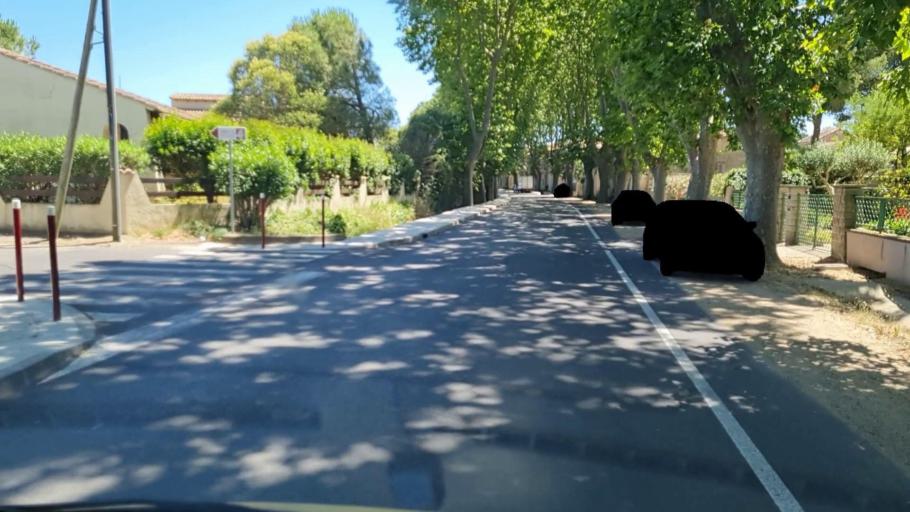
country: FR
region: Languedoc-Roussillon
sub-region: Departement du Gard
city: Le Cailar
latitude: 43.6796
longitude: 4.2353
